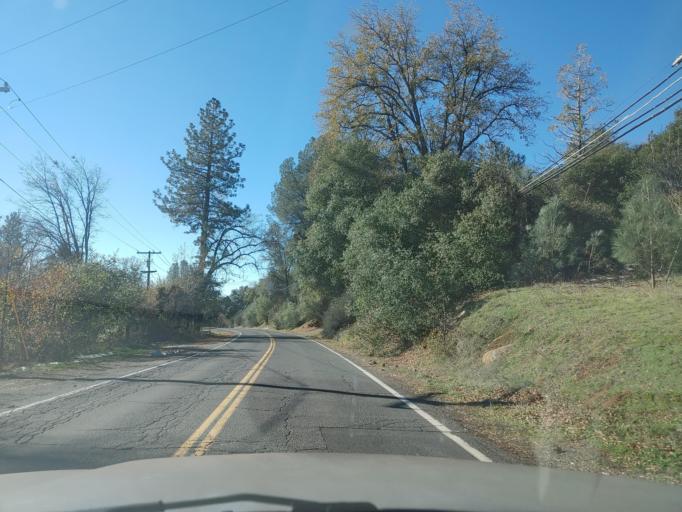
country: US
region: California
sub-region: Tuolumne County
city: Mono Vista
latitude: 37.9951
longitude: -120.2730
